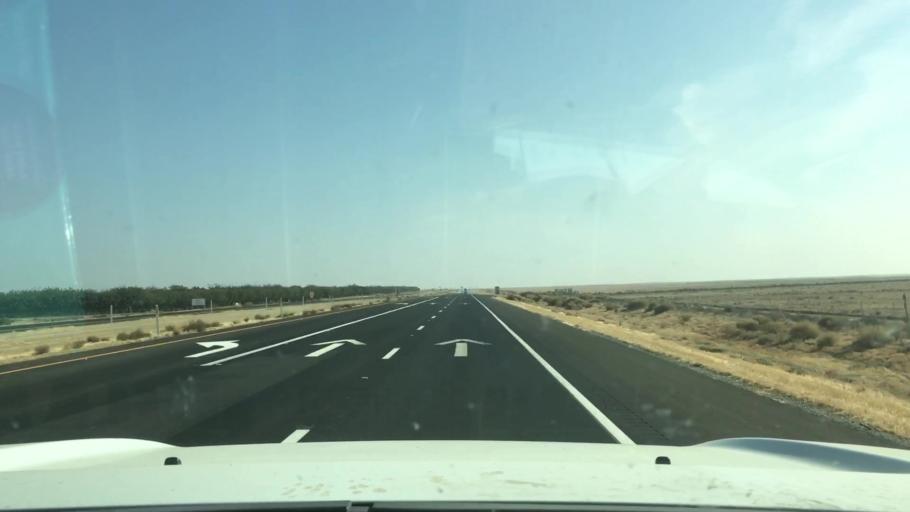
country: US
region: California
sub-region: Kern County
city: Lost Hills
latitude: 35.6202
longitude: -119.9768
